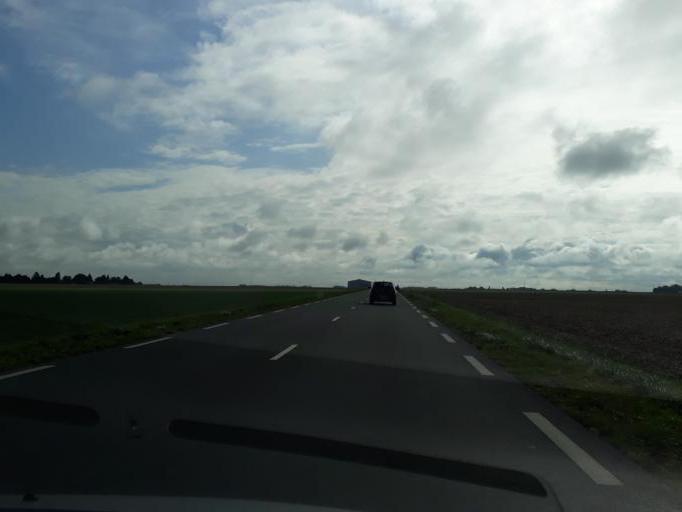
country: FR
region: Centre
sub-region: Departement d'Eure-et-Loir
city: Chateaudun
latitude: 48.0515
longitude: 1.4326
